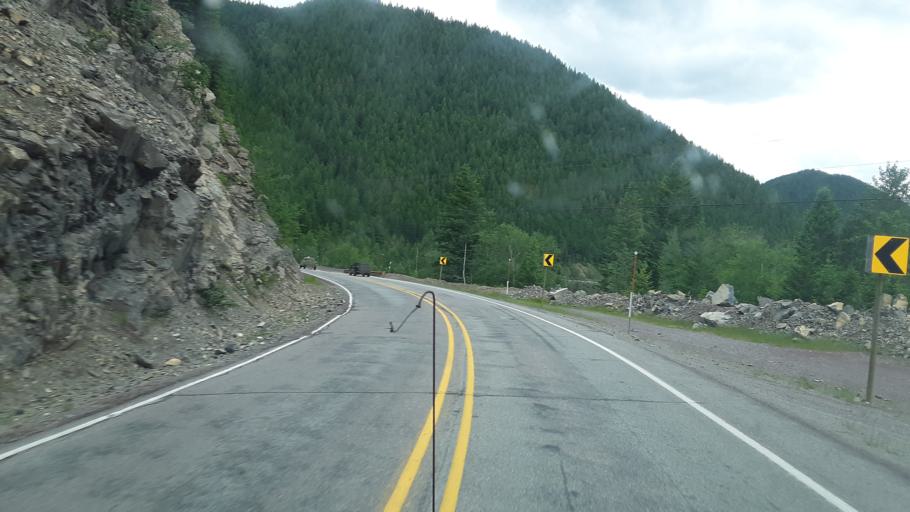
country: US
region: Montana
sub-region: Flathead County
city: Columbia Falls
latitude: 48.4987
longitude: -113.9207
